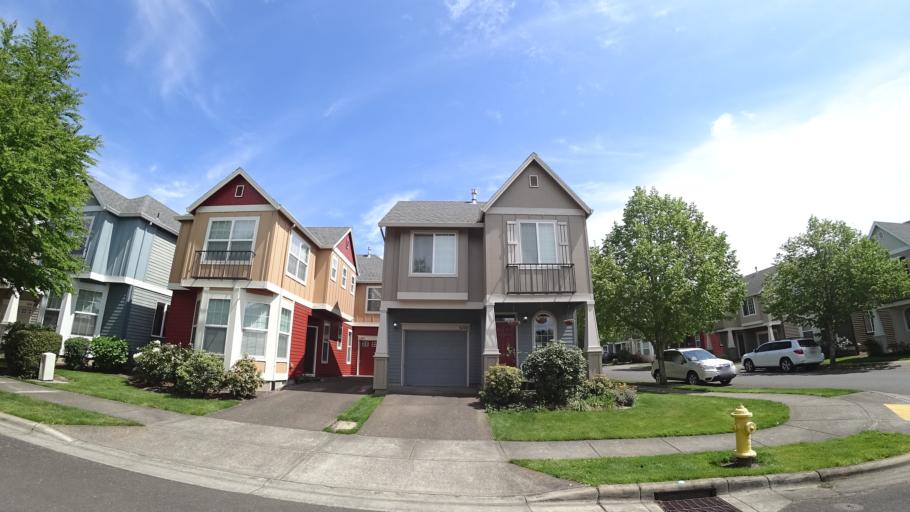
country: US
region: Oregon
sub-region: Washington County
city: Aloha
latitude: 45.4745
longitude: -122.8913
